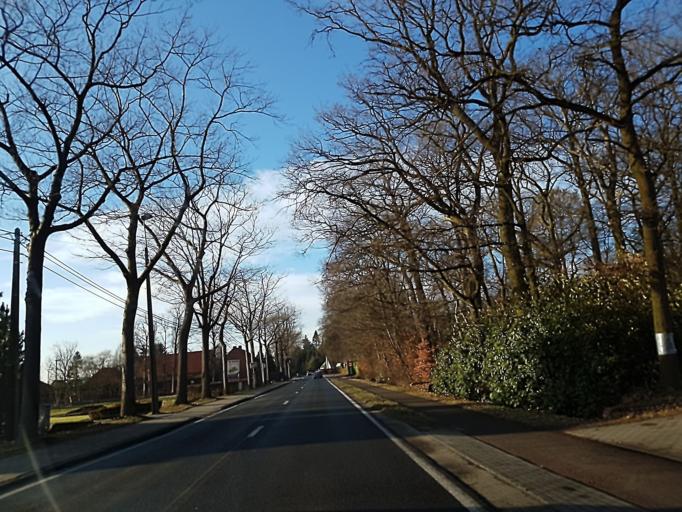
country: BE
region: Flanders
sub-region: Provincie Antwerpen
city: Oud-Turnhout
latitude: 51.3113
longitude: 4.9989
